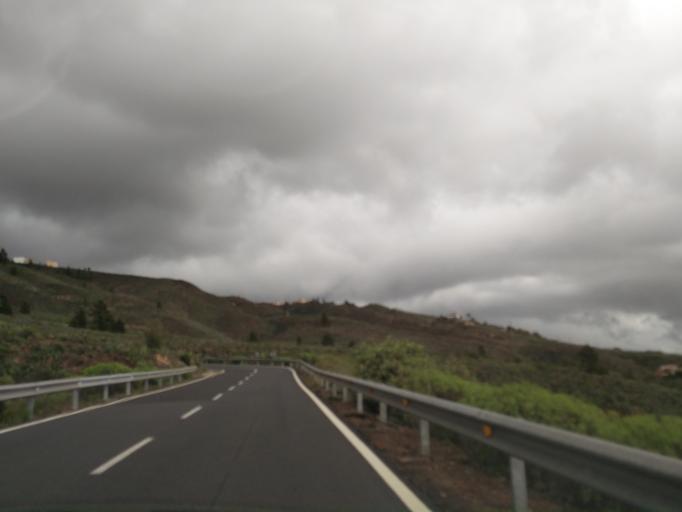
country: ES
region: Canary Islands
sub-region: Provincia de Santa Cruz de Tenerife
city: Arona
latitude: 28.1127
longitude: -16.6832
